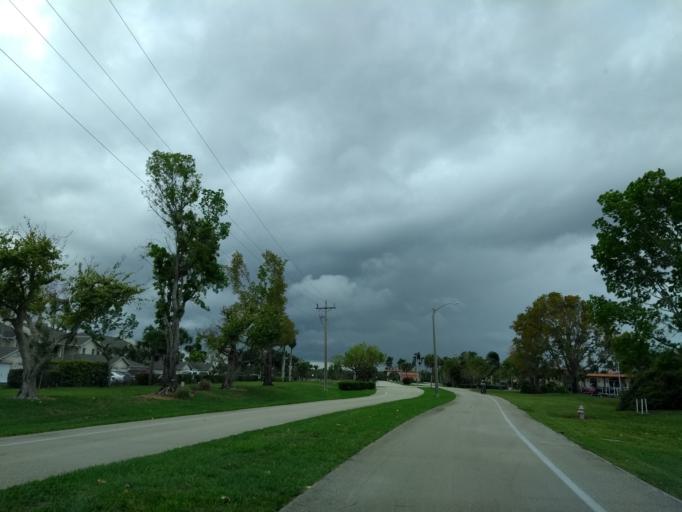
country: US
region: Florida
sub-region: Collier County
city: Marco
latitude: 25.9557
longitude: -81.5124
